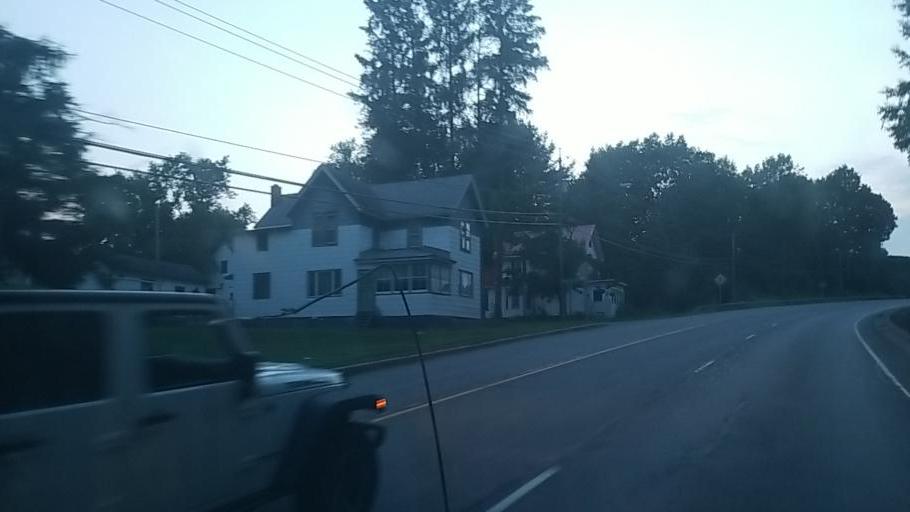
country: US
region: New York
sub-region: Montgomery County
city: Fonda
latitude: 42.9582
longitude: -74.3842
